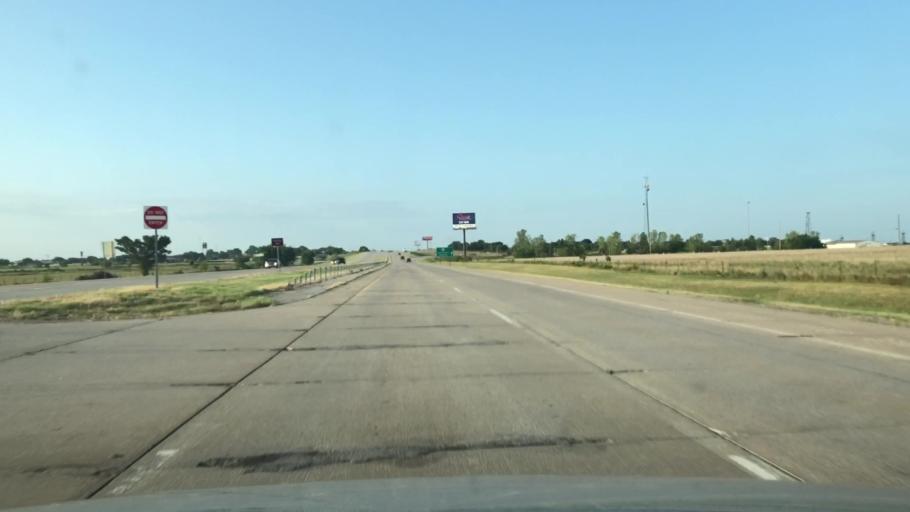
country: US
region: Oklahoma
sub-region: Osage County
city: Skiatook
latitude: 36.3730
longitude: -95.9207
